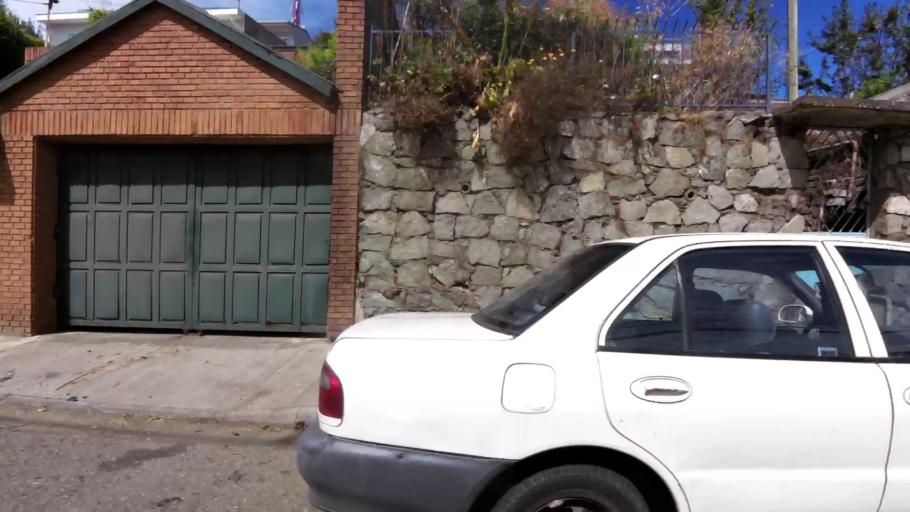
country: CL
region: Biobio
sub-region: Provincia de Concepcion
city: Talcahuano
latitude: -36.7173
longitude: -73.1144
